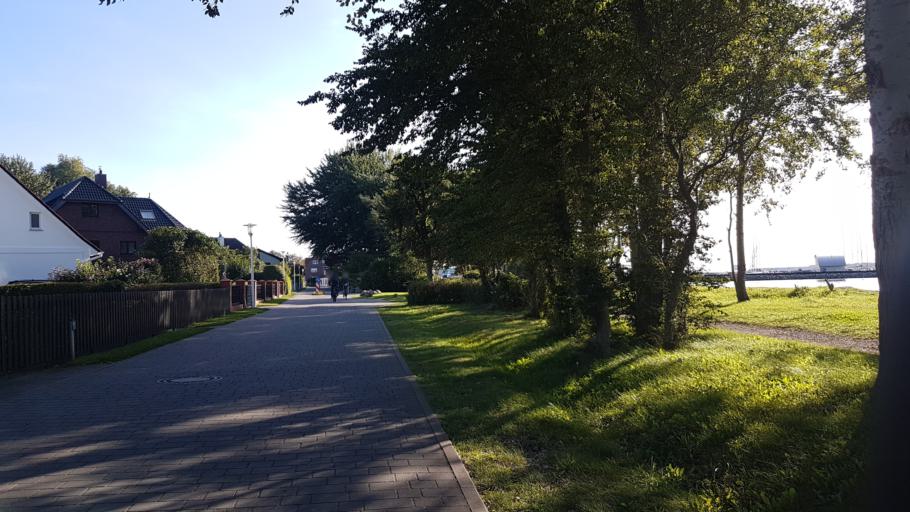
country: DE
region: Mecklenburg-Vorpommern
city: Wiek
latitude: 54.6243
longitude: 13.2875
